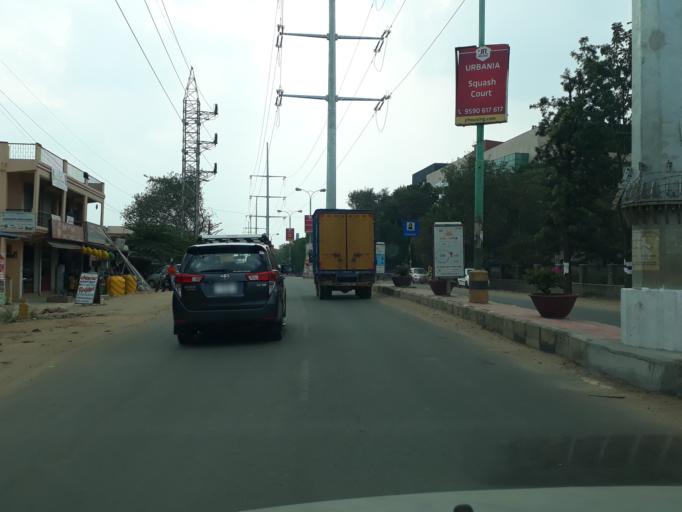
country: IN
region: Karnataka
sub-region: Bangalore Urban
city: Anekal
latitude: 12.8089
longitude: 77.6641
